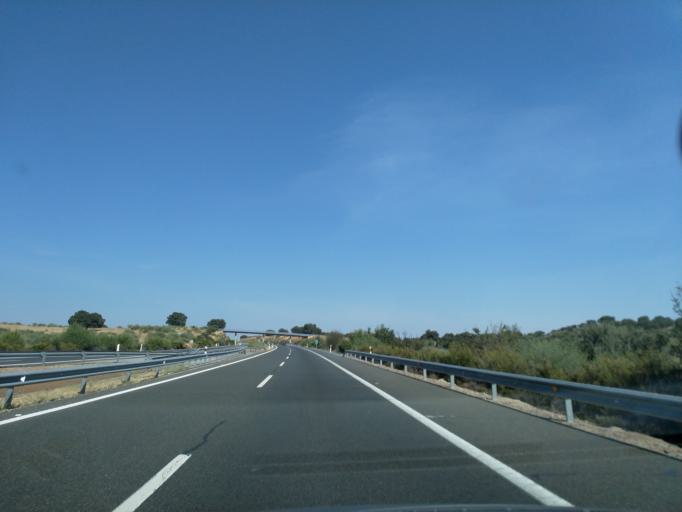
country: ES
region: Extremadura
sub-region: Provincia de Caceres
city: Aldea del Cano
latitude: 39.3105
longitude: -6.3276
